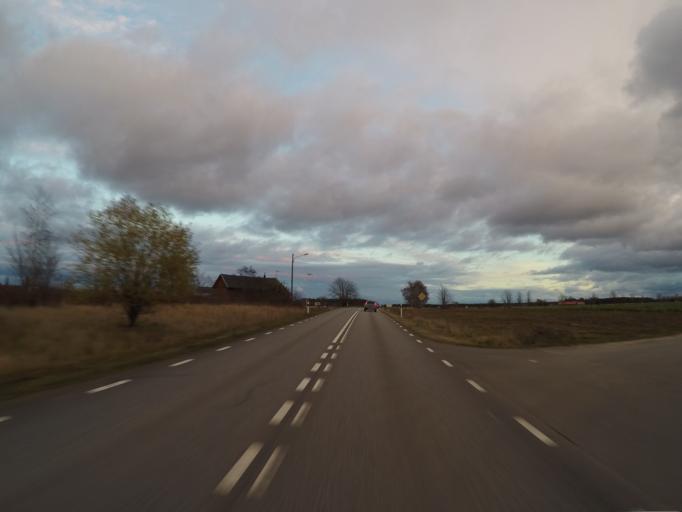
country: SE
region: Skane
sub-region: Kristianstads Kommun
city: Degeberga
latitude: 55.8963
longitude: 14.0766
